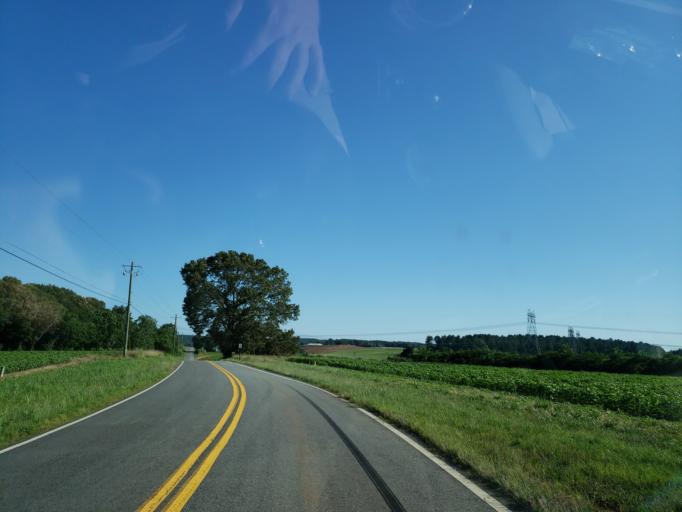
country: US
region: Georgia
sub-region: Bartow County
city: Euharlee
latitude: 34.1081
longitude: -84.9008
